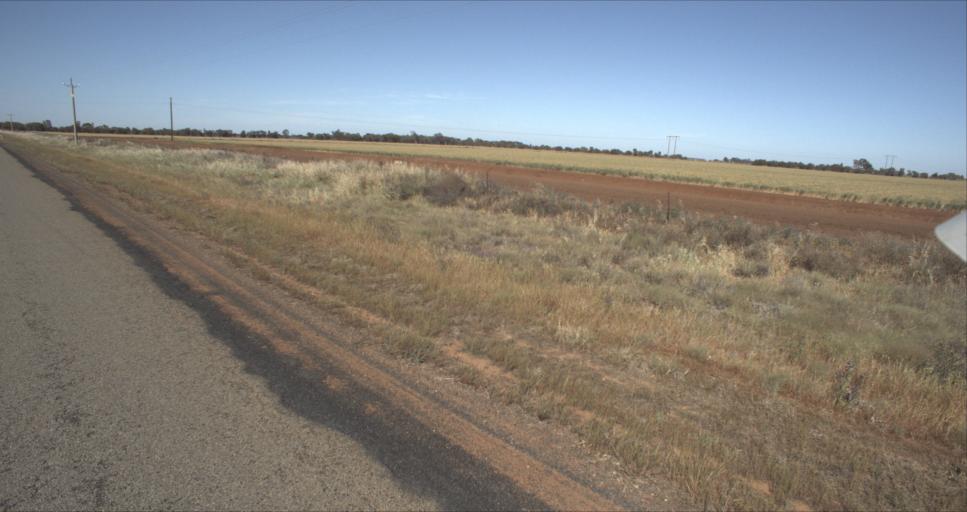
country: AU
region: New South Wales
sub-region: Leeton
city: Leeton
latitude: -34.5577
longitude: 146.2660
